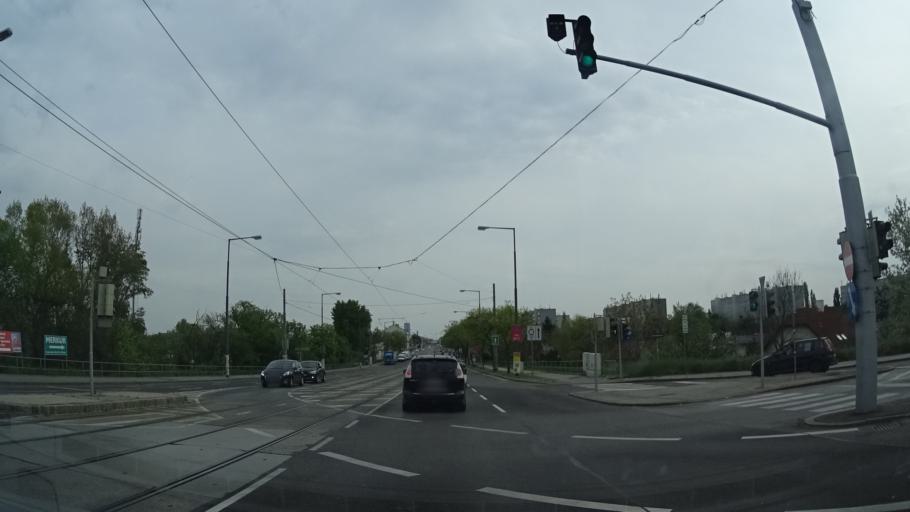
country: AT
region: Lower Austria
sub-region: Politischer Bezirk Korneuburg
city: Langenzersdorf
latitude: 48.2813
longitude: 16.3863
